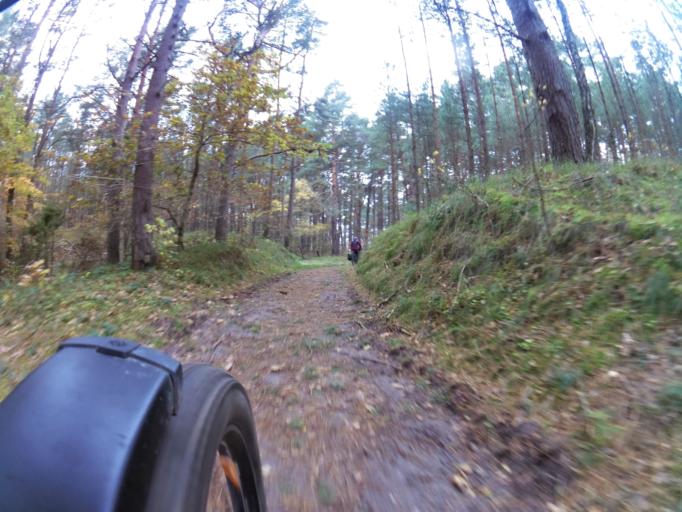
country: PL
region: Pomeranian Voivodeship
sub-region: Powiat pucki
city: Krokowa
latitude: 54.8302
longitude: 18.1253
